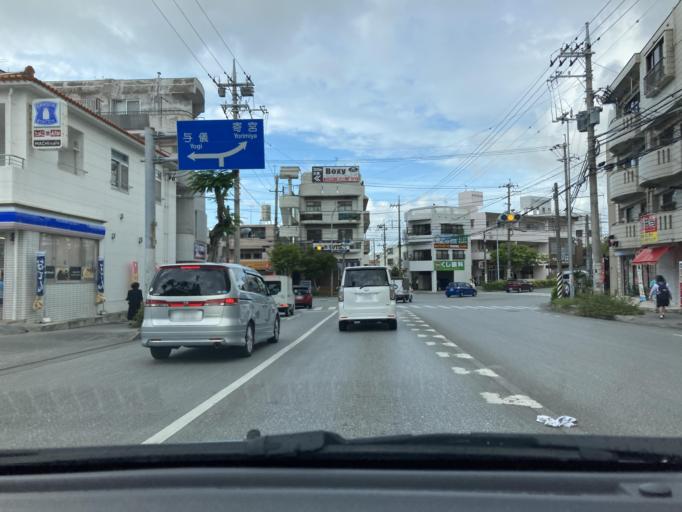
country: JP
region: Okinawa
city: Naha-shi
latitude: 26.2016
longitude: 127.6973
